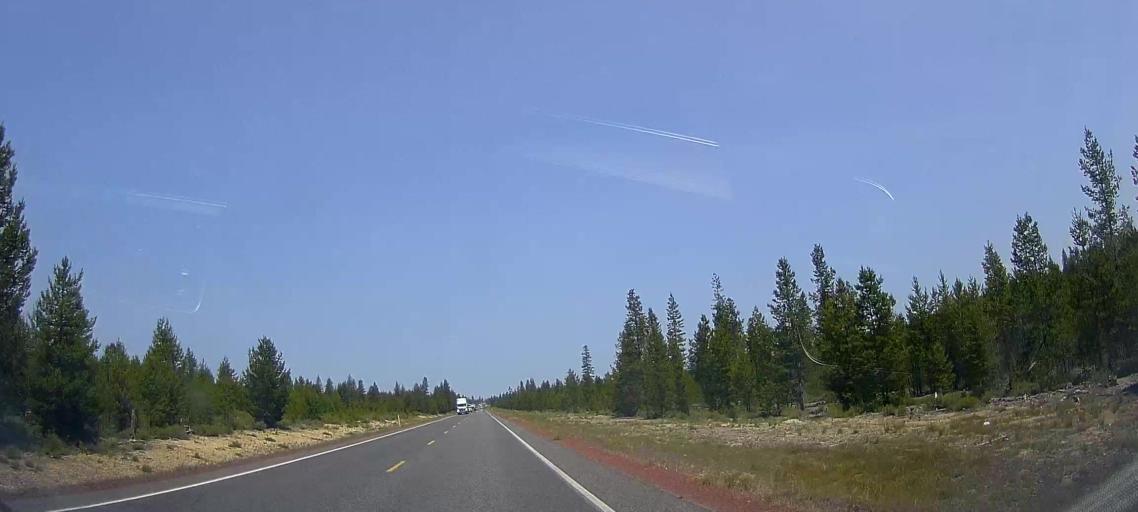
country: US
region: Oregon
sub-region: Deschutes County
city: La Pine
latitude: 43.3893
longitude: -121.7284
